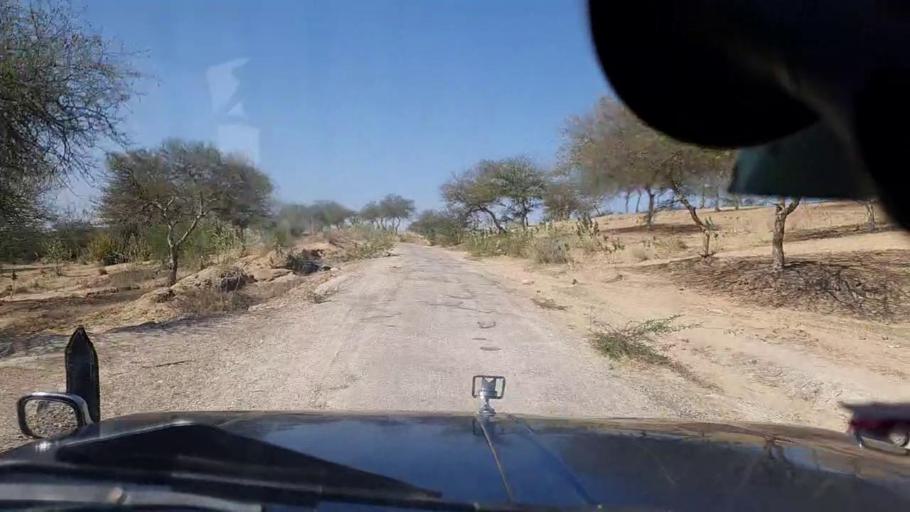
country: PK
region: Sindh
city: Mithi
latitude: 24.6116
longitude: 69.7017
